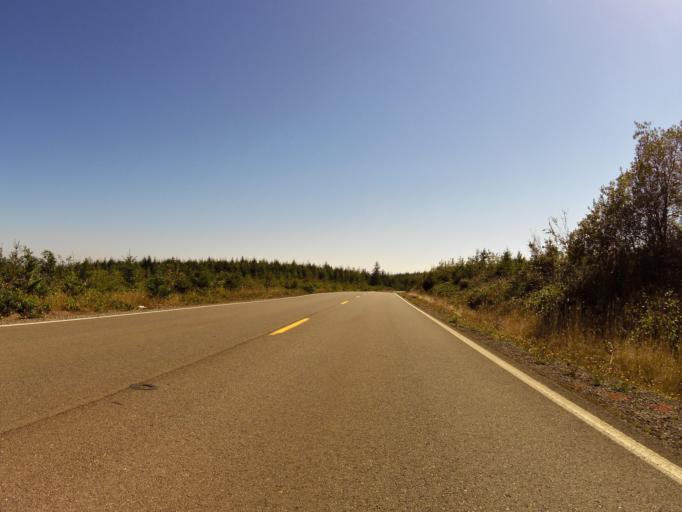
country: US
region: Oregon
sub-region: Coos County
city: Barview
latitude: 43.2587
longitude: -124.3391
